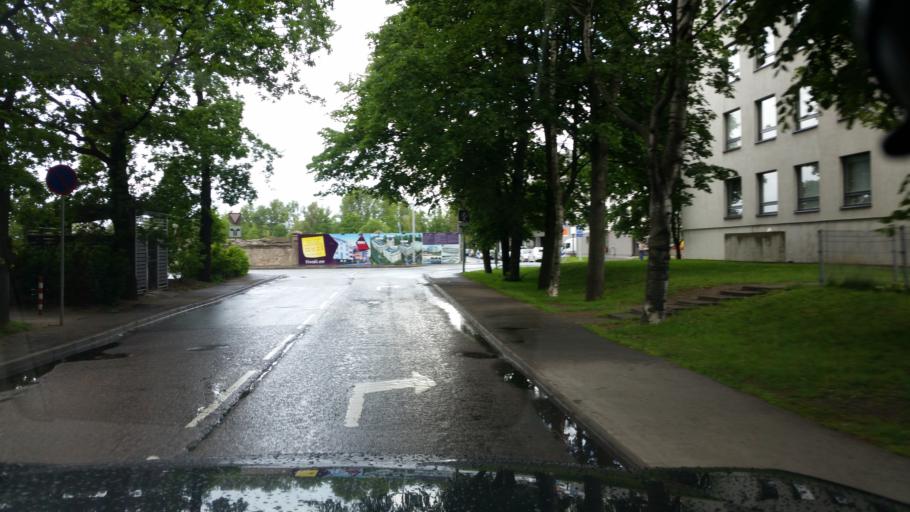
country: EE
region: Harju
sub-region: Tallinna linn
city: Tallinn
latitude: 59.4410
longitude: 24.7816
